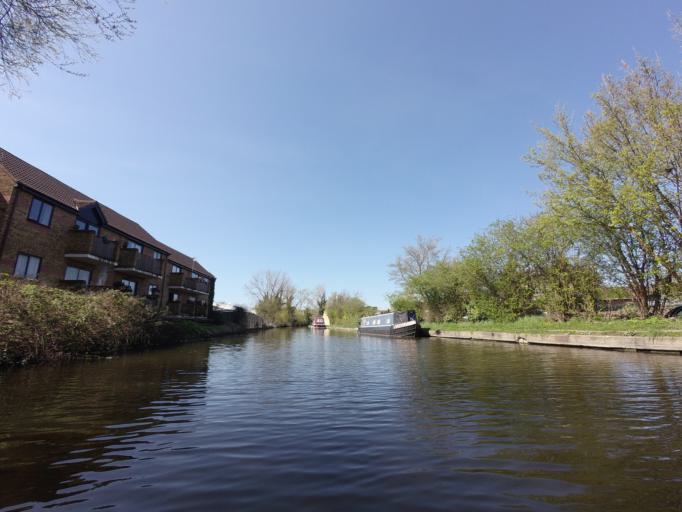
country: GB
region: England
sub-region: Greater London
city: West Drayton
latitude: 51.5120
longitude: -0.4745
